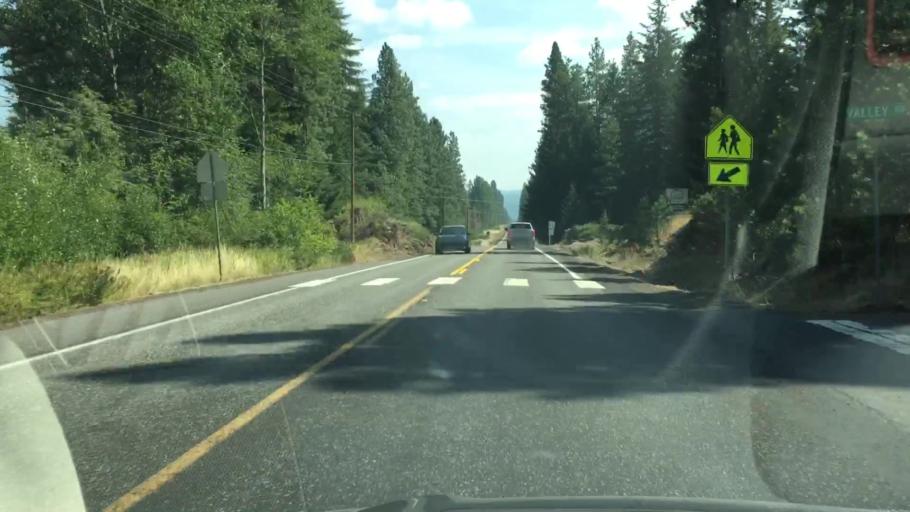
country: US
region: Washington
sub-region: Klickitat County
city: White Salmon
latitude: 45.9871
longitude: -121.5151
